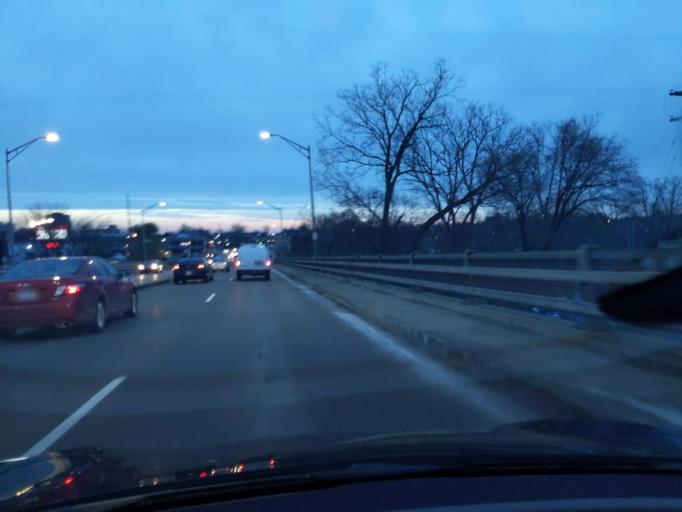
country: US
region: Michigan
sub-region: Ingham County
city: Lansing
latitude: 42.7200
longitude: -84.5454
